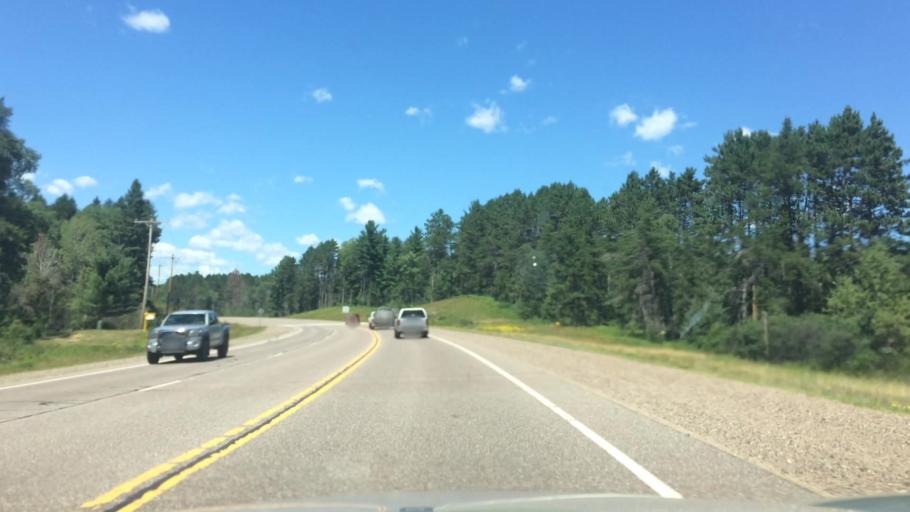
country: US
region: Wisconsin
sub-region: Lincoln County
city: Tomahawk
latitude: 45.6562
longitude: -89.7051
